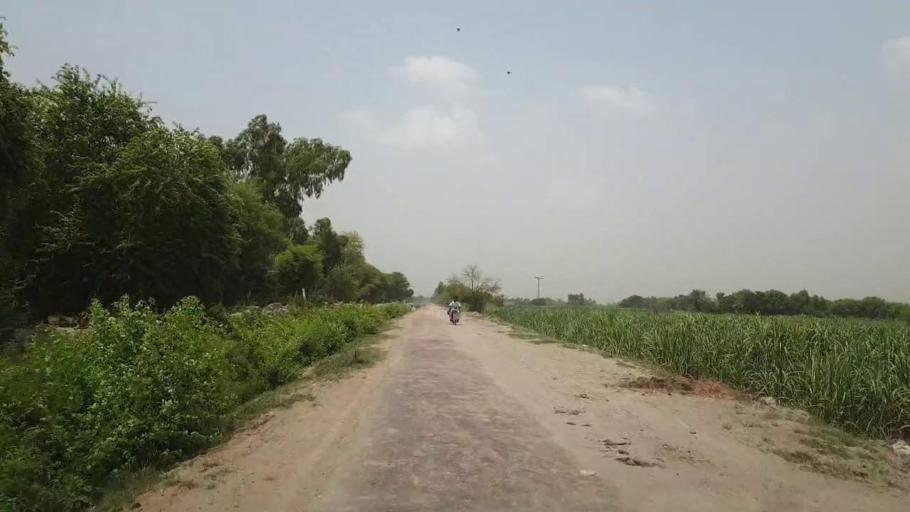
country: PK
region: Sindh
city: Sobhadero
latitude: 27.4363
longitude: 68.4045
